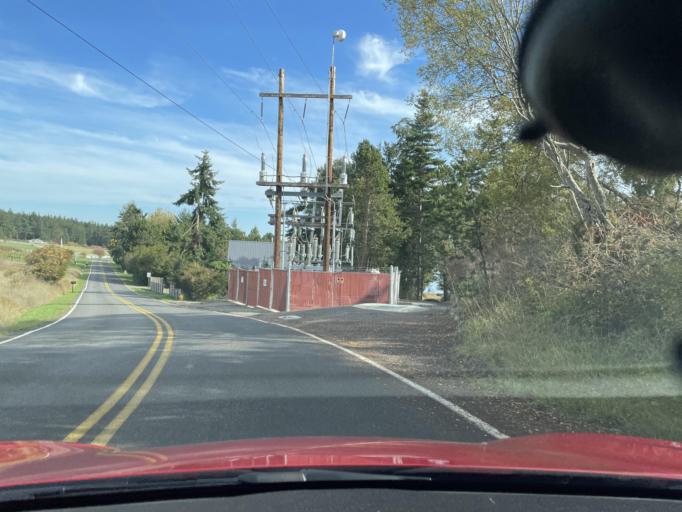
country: US
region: Washington
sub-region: San Juan County
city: Friday Harbor
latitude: 48.5182
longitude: -122.9823
